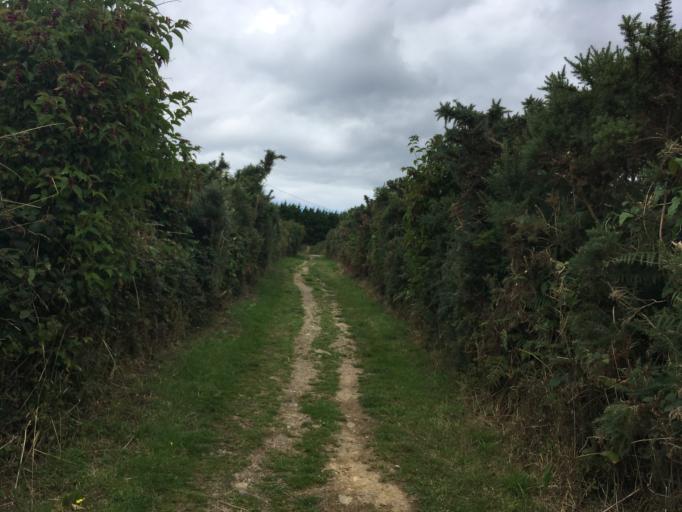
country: IE
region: Munster
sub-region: County Cork
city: Crosshaven
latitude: 51.8068
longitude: -8.2792
